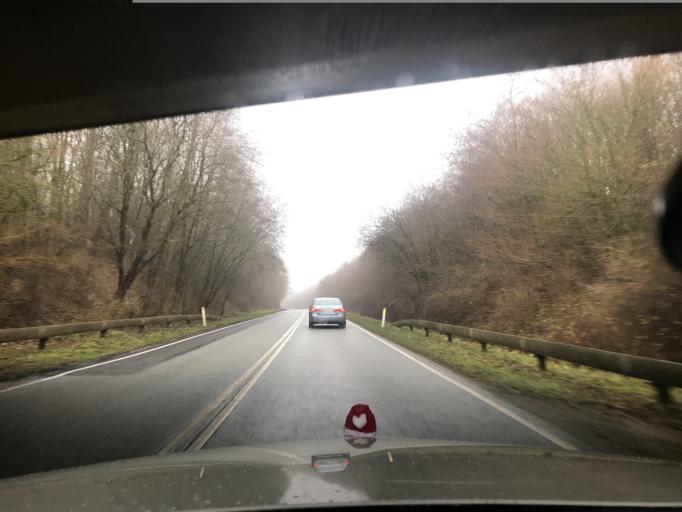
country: DK
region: South Denmark
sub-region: Aabenraa Kommune
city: Aabenraa
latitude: 55.0012
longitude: 9.4388
